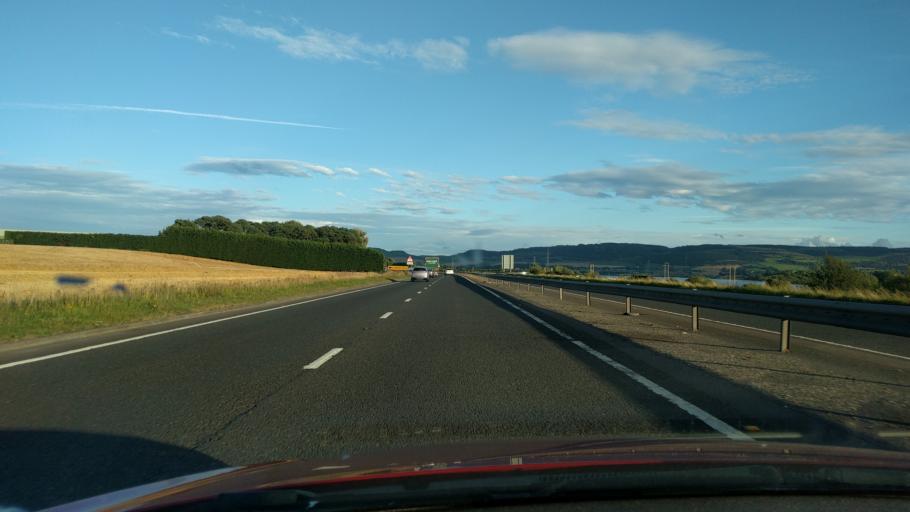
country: GB
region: Scotland
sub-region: Perth and Kinross
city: Abernethy
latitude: 56.3764
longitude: -3.3385
